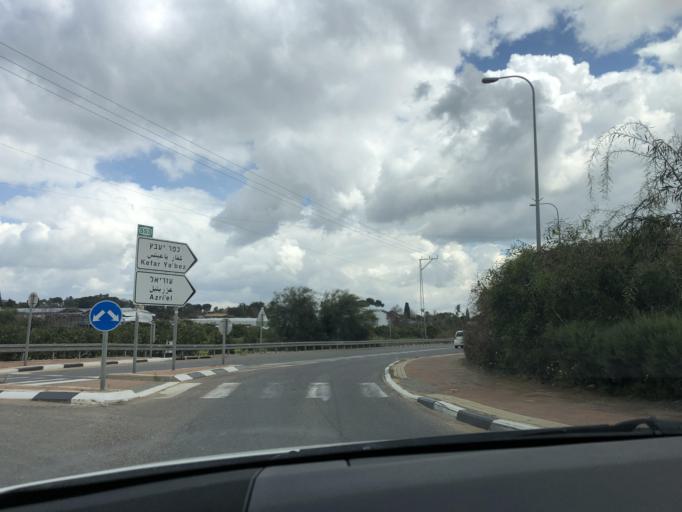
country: IL
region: Central District
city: Tel Mond
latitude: 32.2615
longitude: 34.9252
